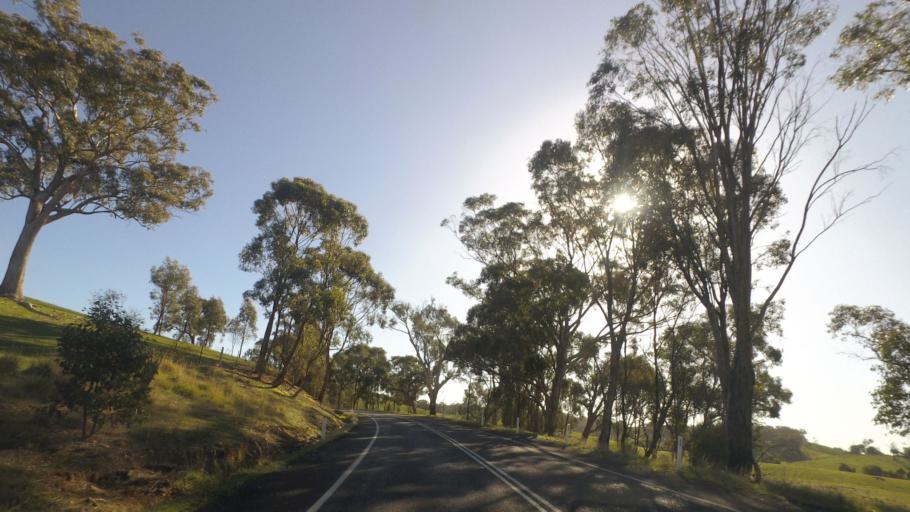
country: AU
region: Victoria
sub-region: Greater Bendigo
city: Kennington
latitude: -36.9138
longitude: 144.3331
